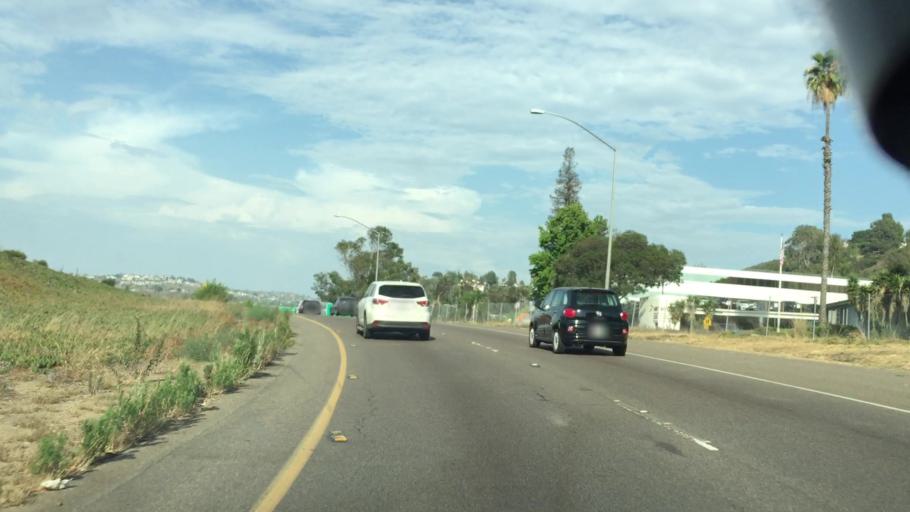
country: US
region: California
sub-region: San Diego County
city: San Diego
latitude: 32.7780
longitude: -117.1094
